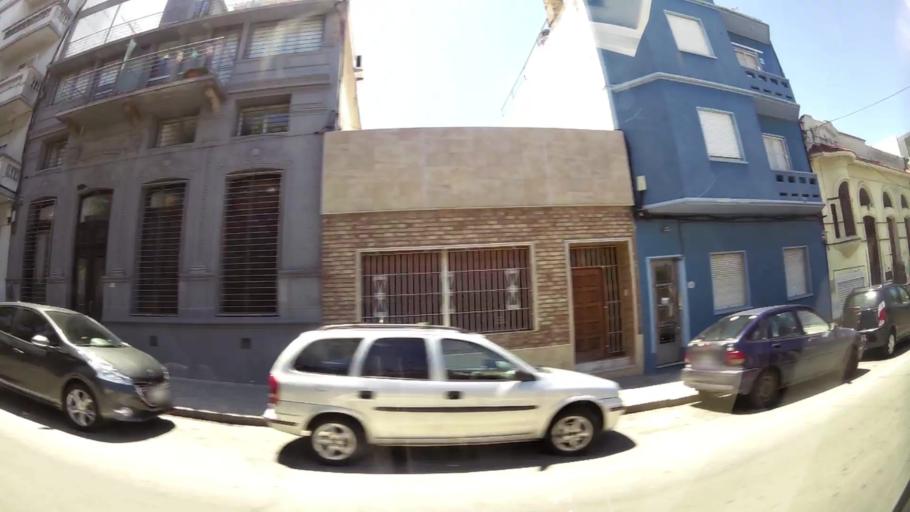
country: UY
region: Montevideo
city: Montevideo
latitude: -34.9090
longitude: -56.1741
